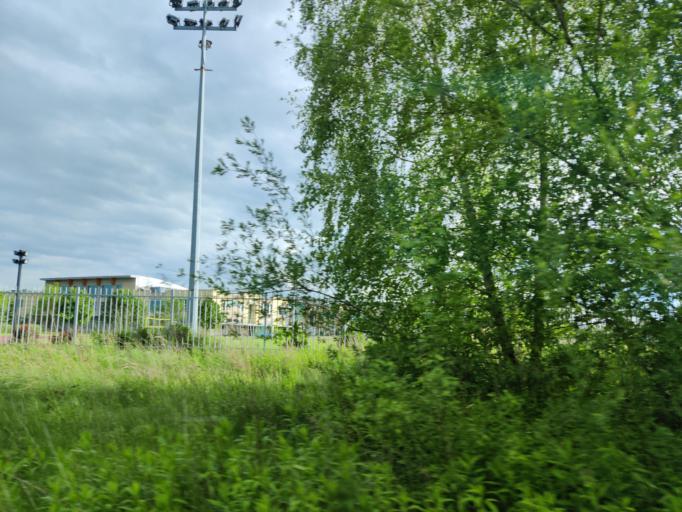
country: PL
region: Masovian Voivodeship
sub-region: Powiat piaseczynski
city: Konstancin-Jeziorna
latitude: 52.1154
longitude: 21.1167
